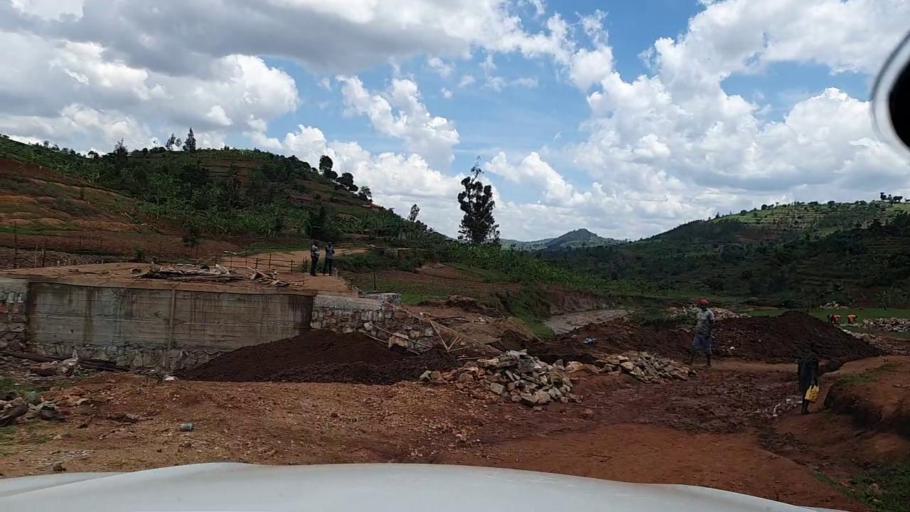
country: RW
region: Southern Province
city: Butare
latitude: -2.7430
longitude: 29.7687
